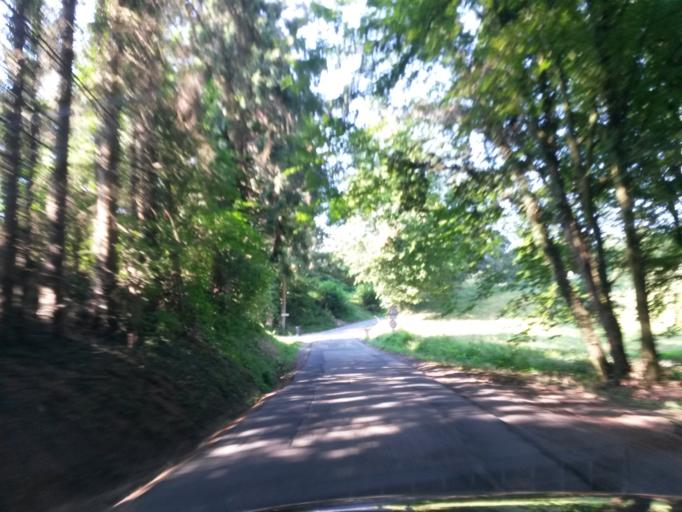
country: DE
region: North Rhine-Westphalia
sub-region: Regierungsbezirk Koln
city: Rosrath
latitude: 50.8778
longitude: 7.2090
